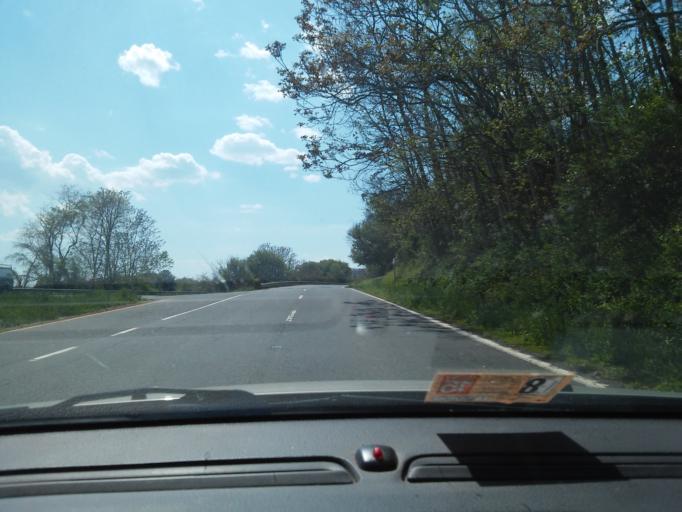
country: US
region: Virginia
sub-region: Rappahannock County
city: Washington
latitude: 38.7135
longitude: -78.1366
